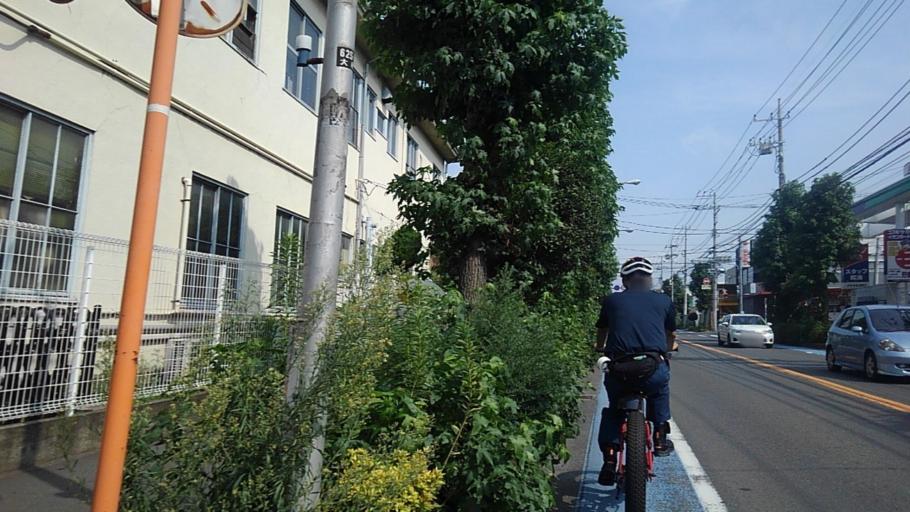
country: JP
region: Kanagawa
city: Minami-rinkan
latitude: 35.4779
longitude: 139.4609
